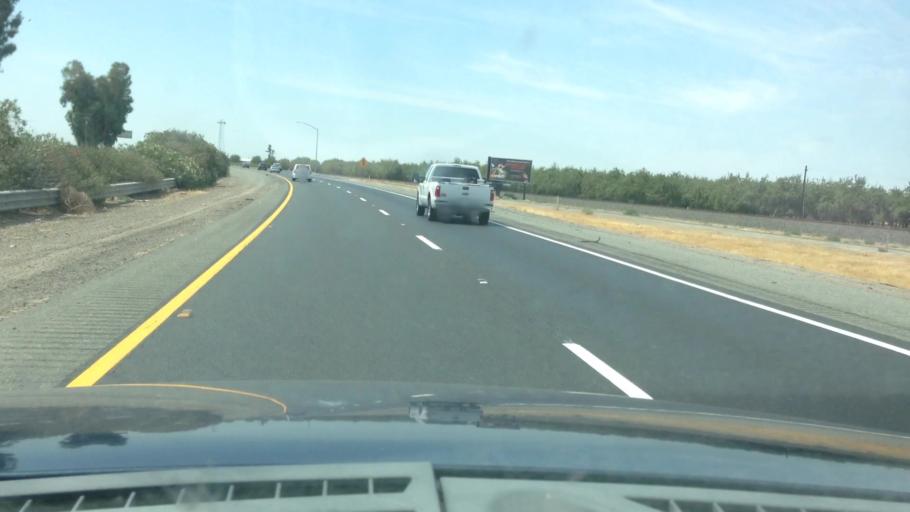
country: US
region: California
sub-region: Tulare County
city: Earlimart
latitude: 35.8711
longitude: -119.2709
